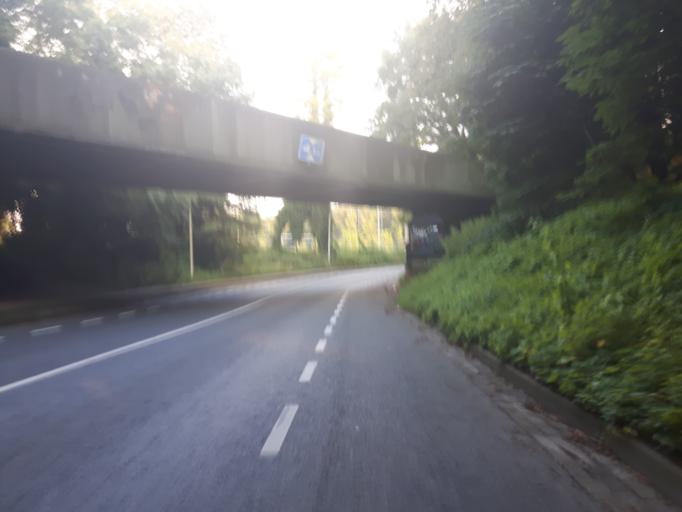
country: NL
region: Overijssel
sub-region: Gemeente Hengelo
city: Hengelo
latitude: 52.2485
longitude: 6.8031
